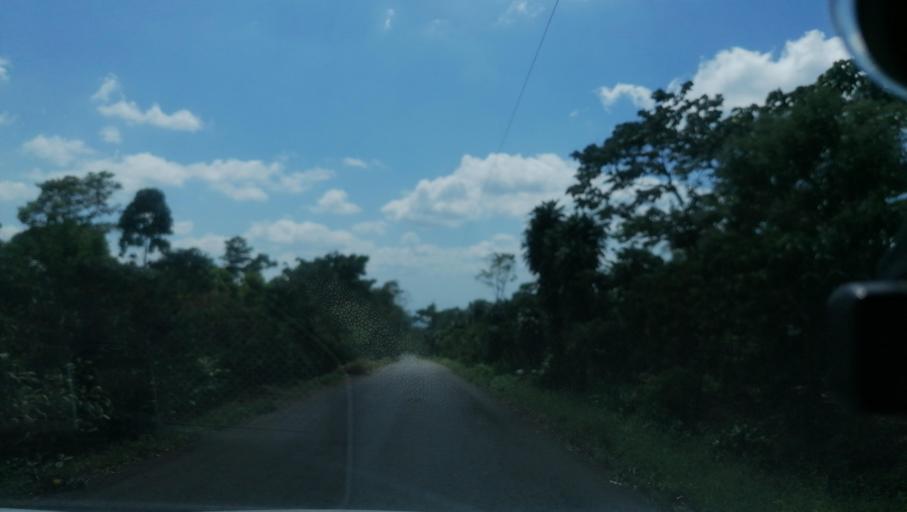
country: MX
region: Chiapas
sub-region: Cacahoatan
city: Benito Juarez
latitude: 15.0522
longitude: -92.1476
